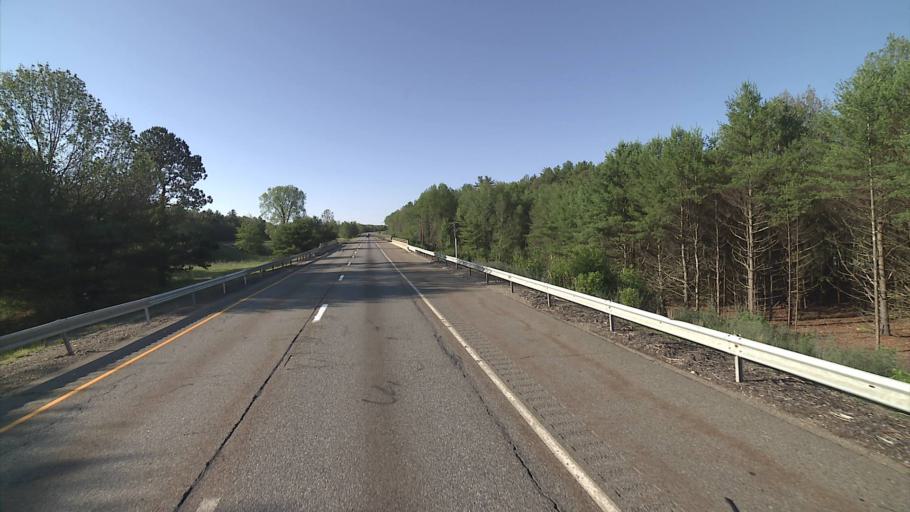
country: US
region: Massachusetts
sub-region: Worcester County
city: Webster
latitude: 42.0091
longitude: -71.8554
